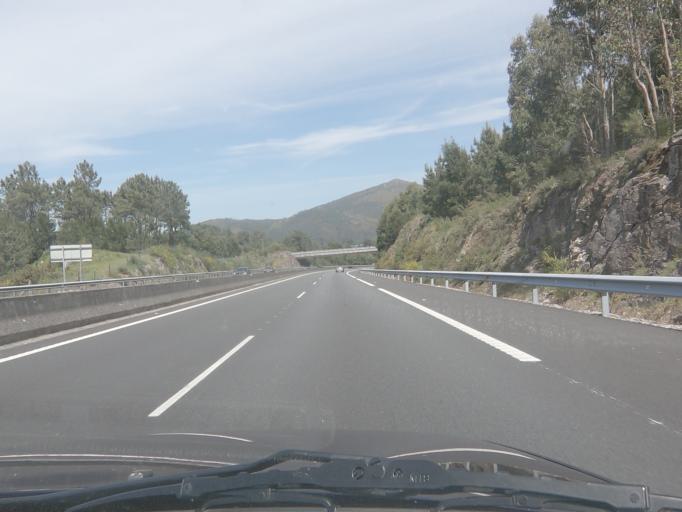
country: ES
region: Galicia
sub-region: Provincia de Pontevedra
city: Valga
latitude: 42.7212
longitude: -8.6410
